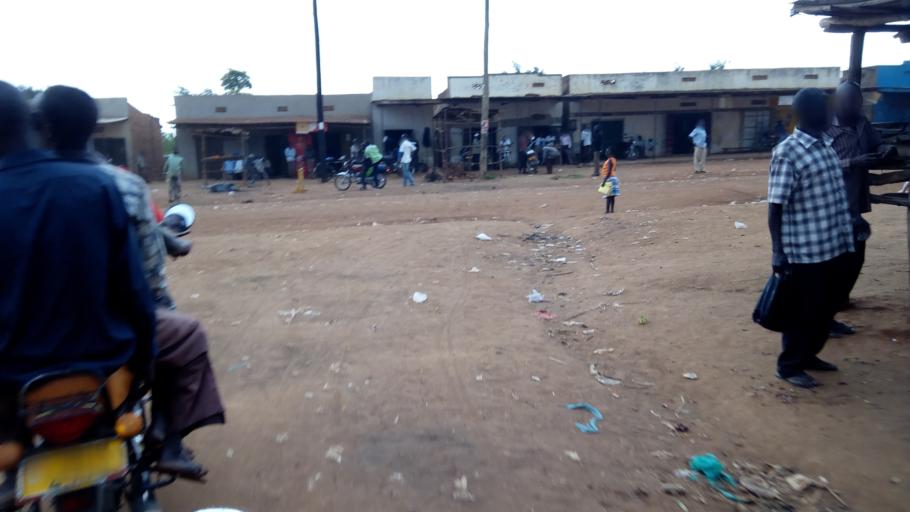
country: UG
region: Eastern Region
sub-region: Mbale District
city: Mbale
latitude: 1.1396
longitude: 34.1110
